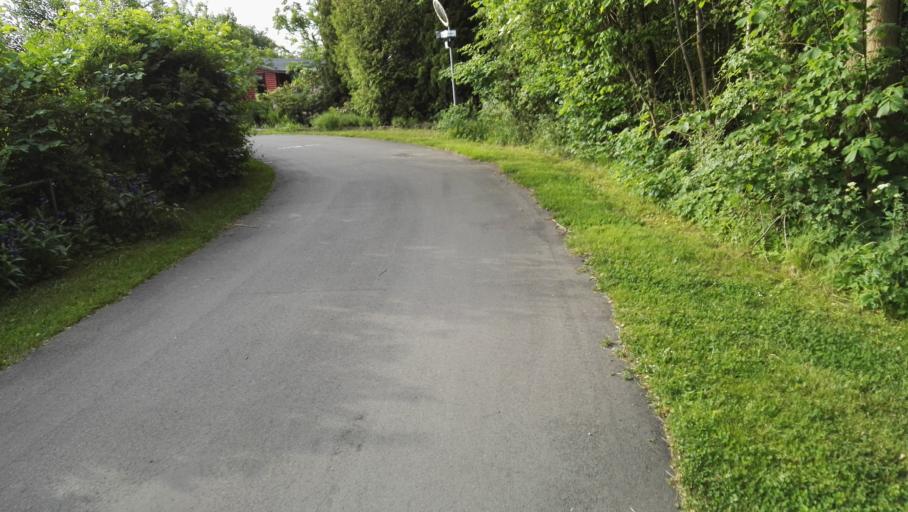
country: DK
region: Capital Region
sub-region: Ballerup Kommune
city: Ballerup
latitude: 55.7184
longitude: 12.3422
